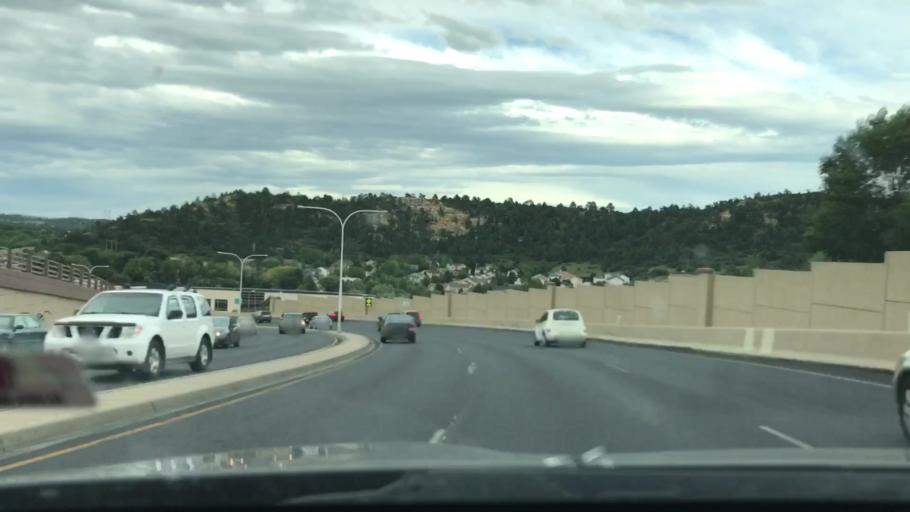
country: US
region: Colorado
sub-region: El Paso County
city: Colorado Springs
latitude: 38.8877
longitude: -104.7907
